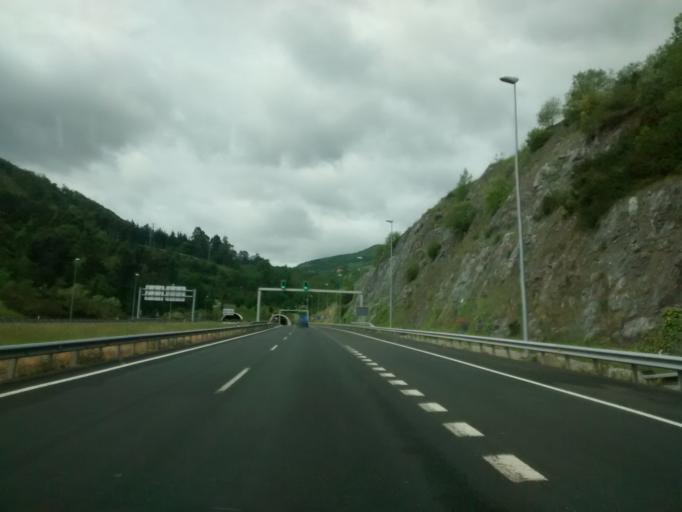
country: ES
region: Cantabria
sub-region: Provincia de Cantabria
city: Los Corrales de Buelna
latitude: 43.2501
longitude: -4.0775
